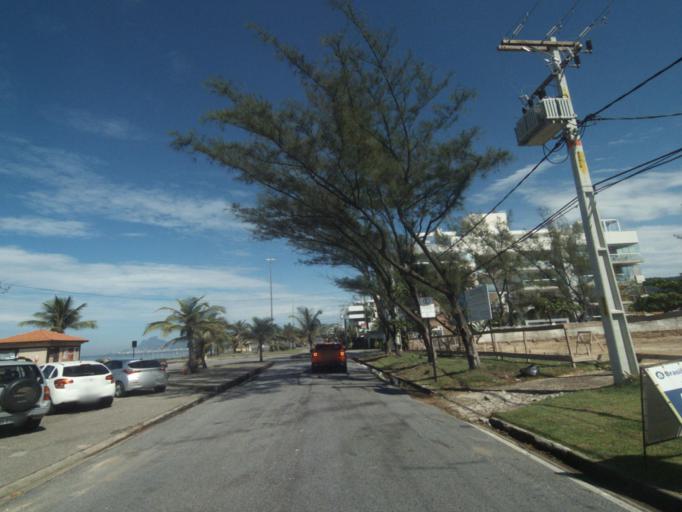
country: BR
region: Rio de Janeiro
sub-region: Niteroi
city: Niteroi
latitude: -22.9553
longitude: -43.0767
